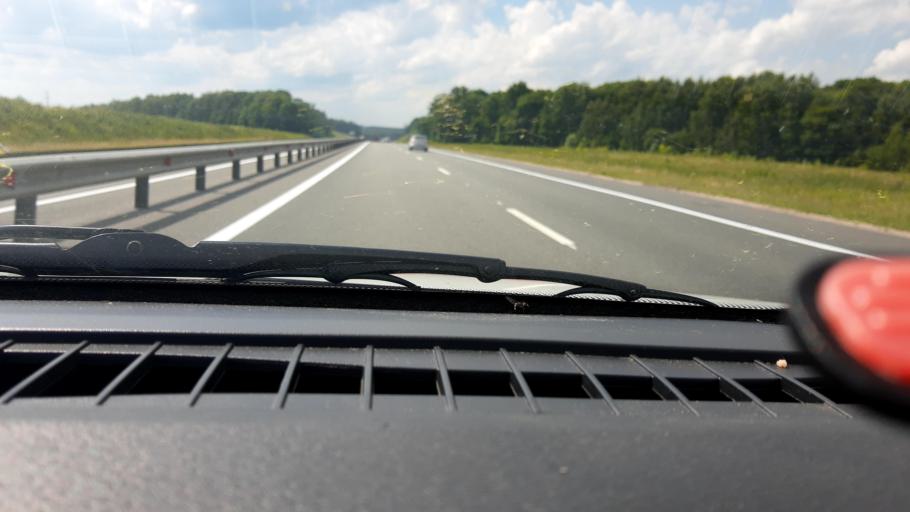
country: RU
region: Nizjnij Novgorod
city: Kstovo
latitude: 56.1006
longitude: 44.0455
